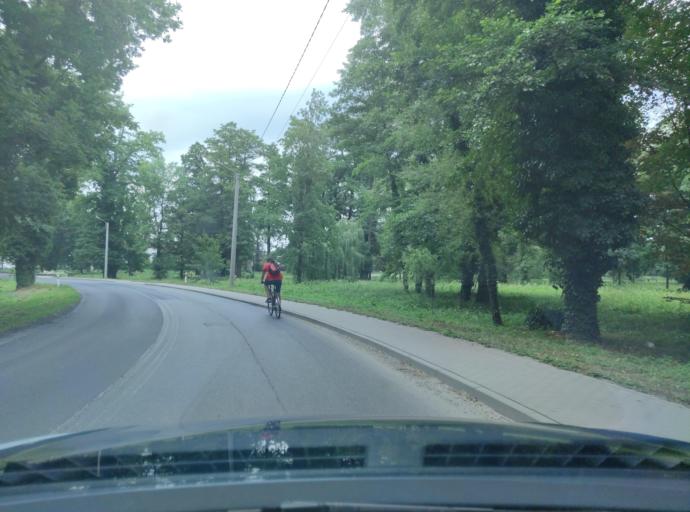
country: PL
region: Opole Voivodeship
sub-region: Powiat strzelecki
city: Strzelce Opolskie
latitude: 50.5077
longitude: 18.3001
